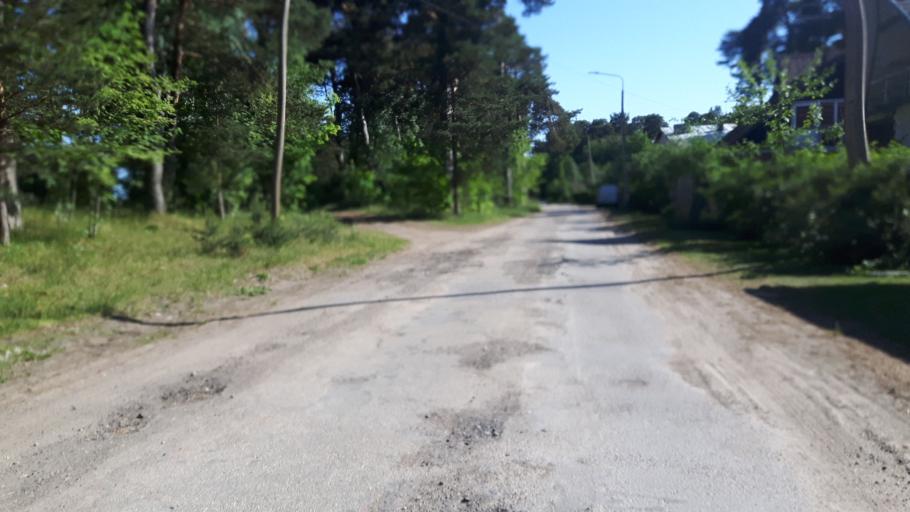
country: LV
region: Salacgrivas
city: Salacgriva
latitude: 57.7453
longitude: 24.3530
